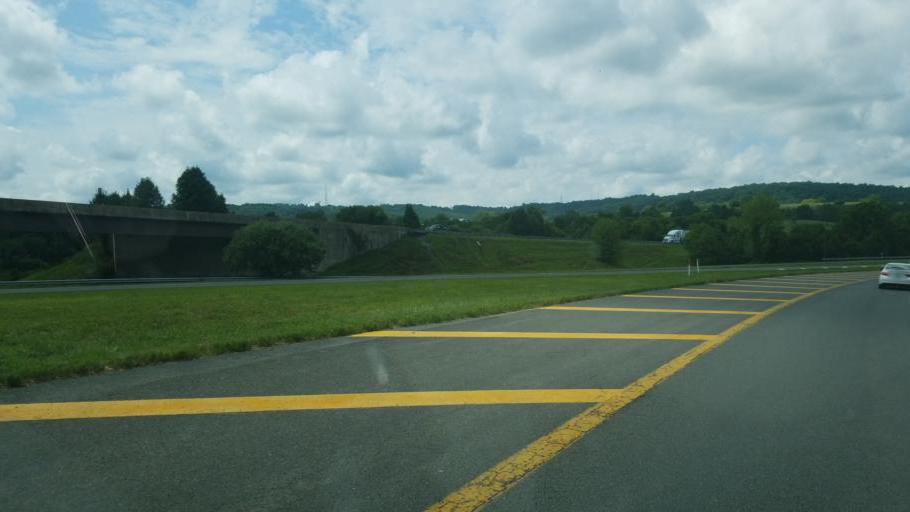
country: US
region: Virginia
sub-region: Fauquier County
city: Warrenton
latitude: 38.7384
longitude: -77.8055
